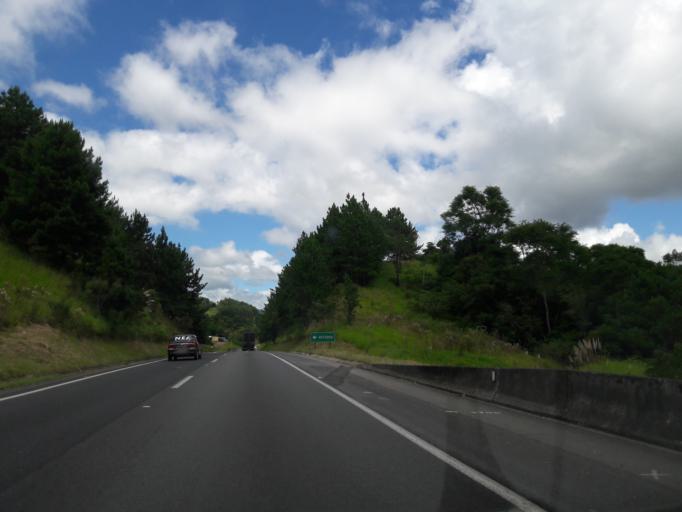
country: BR
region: Parana
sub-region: Campina Grande Do Sul
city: Campina Grande do Sul
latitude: -25.1132
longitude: -48.8536
